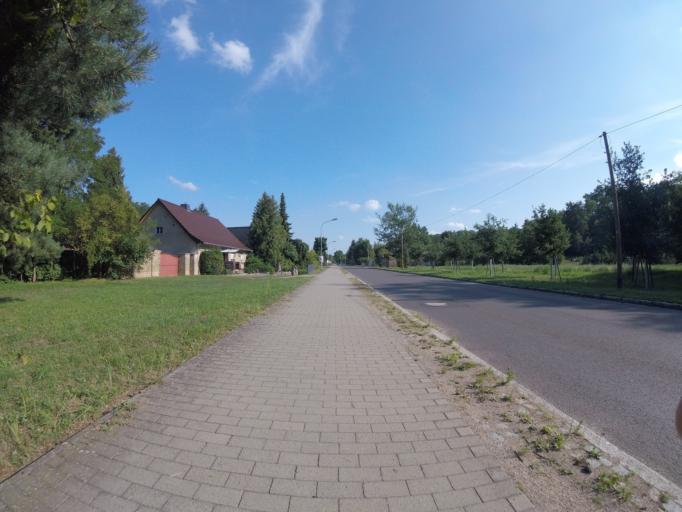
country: DE
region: Brandenburg
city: Bliesdorf
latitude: 52.6935
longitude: 14.1394
